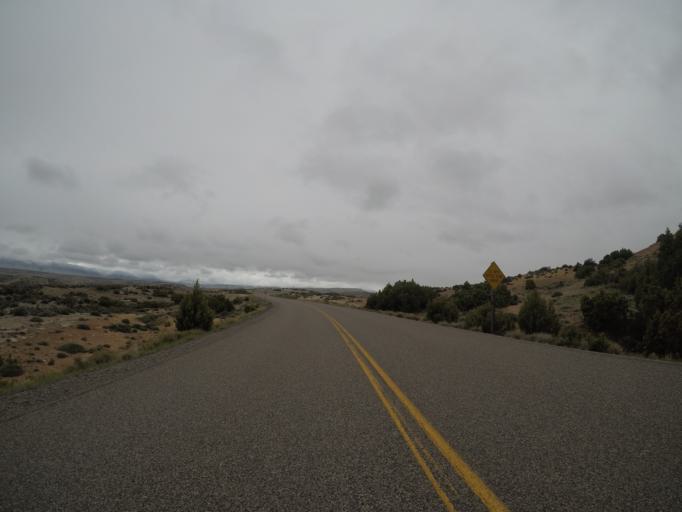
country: US
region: Wyoming
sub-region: Big Horn County
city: Lovell
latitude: 45.0229
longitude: -108.2540
